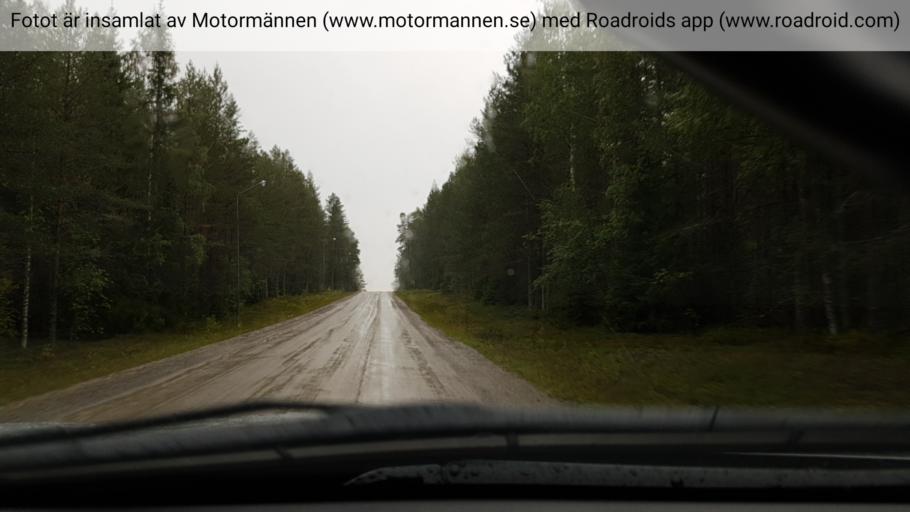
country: SE
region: Vaesterbotten
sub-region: Skelleftea Kommun
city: Burea
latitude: 64.3699
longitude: 21.0854
